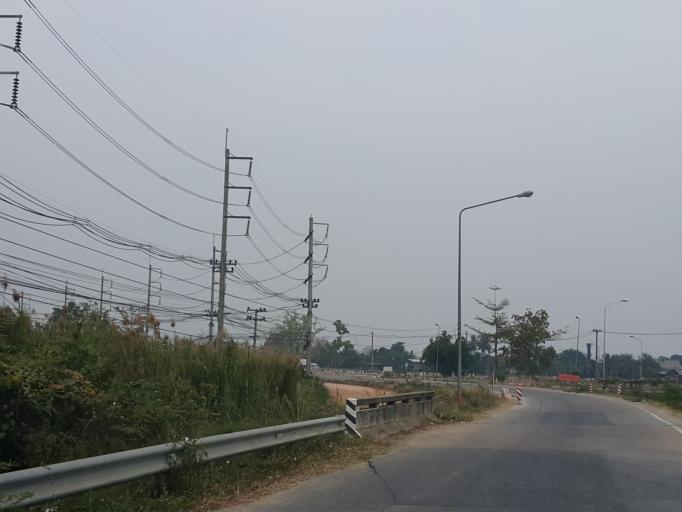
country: TH
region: Chiang Mai
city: Saraphi
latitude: 18.7372
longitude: 99.0384
